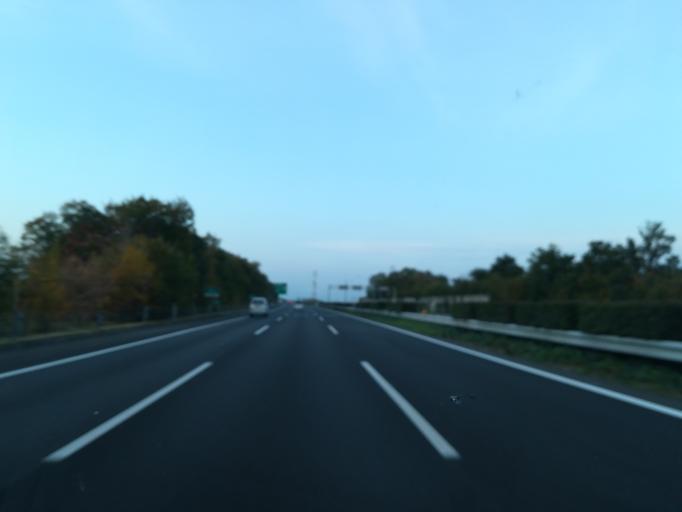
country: JP
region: Gunma
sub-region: Sawa-gun
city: Tamamura
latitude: 36.3018
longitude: 139.0946
